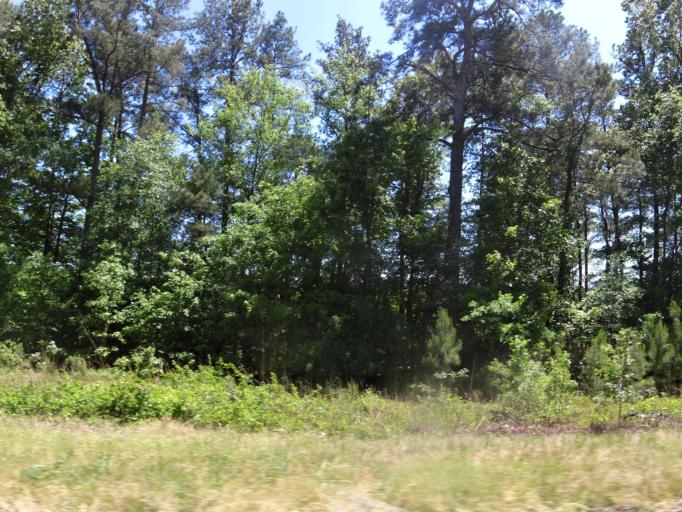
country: US
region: South Carolina
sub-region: Aiken County
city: Warrenville
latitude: 33.5597
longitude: -81.7879
